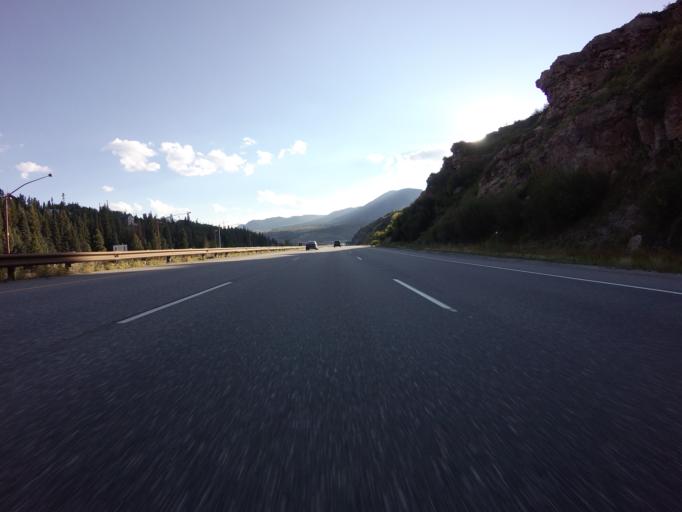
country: US
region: Colorado
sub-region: Summit County
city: Silverthorne
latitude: 39.6343
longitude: -106.0537
